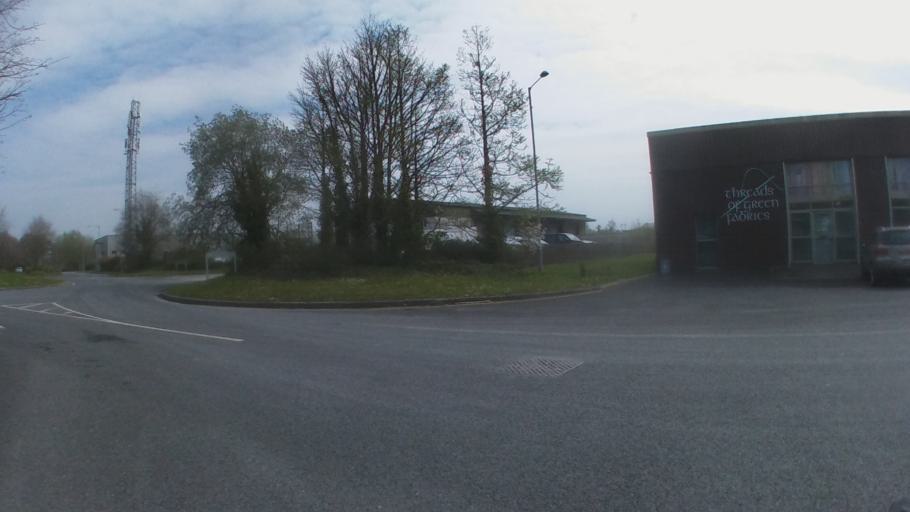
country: IE
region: Leinster
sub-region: Kilkenny
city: Kilkenny
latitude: 52.6437
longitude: -7.2105
